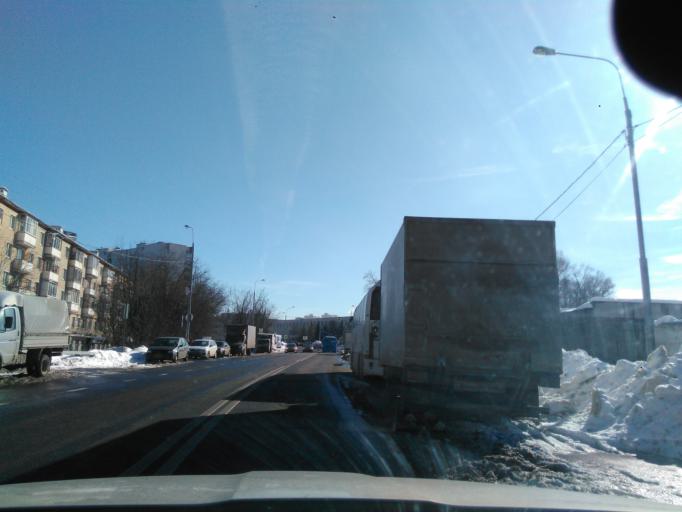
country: RU
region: Moscow
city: Zelenograd
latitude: 55.9867
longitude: 37.1709
